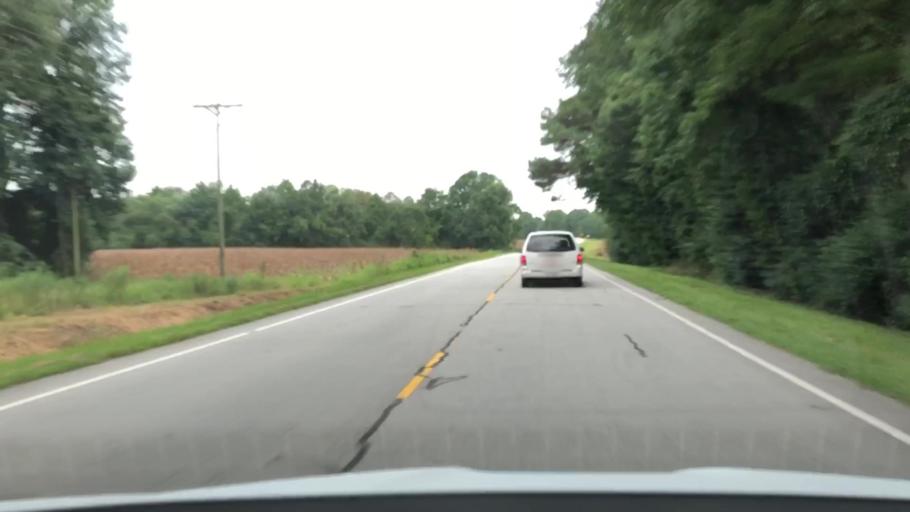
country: US
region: North Carolina
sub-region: Jones County
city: Trenton
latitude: 35.0787
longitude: -77.4107
